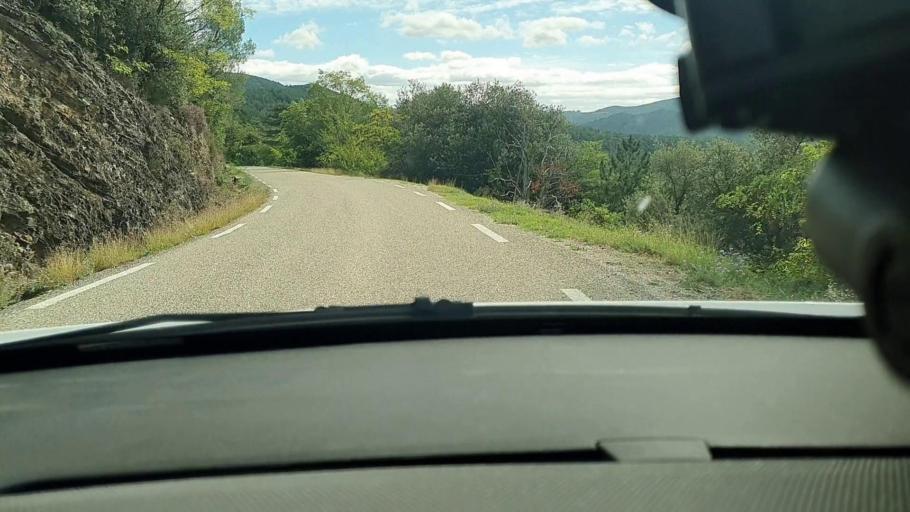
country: FR
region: Languedoc-Roussillon
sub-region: Departement du Gard
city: Branoux-les-Taillades
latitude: 44.3320
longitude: 3.9564
